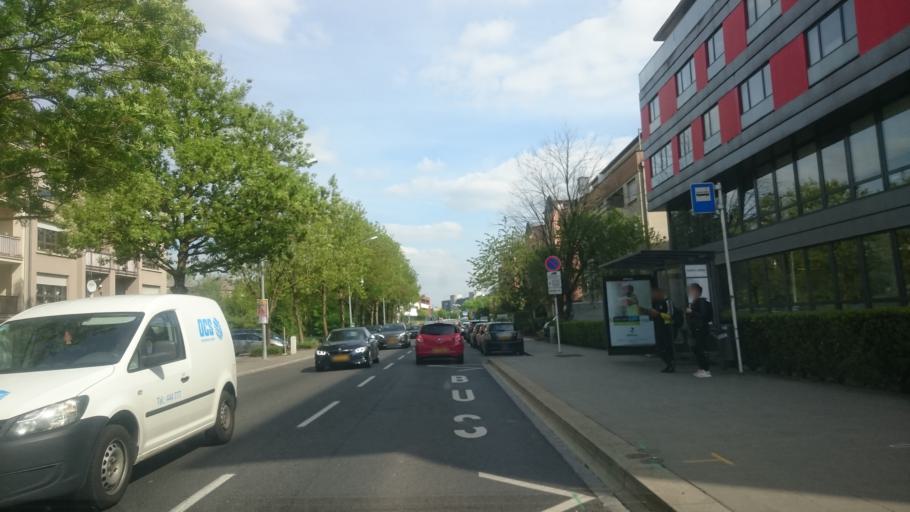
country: LU
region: Luxembourg
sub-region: Canton de Luxembourg
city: Luxembourg
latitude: 49.6017
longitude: 6.1014
